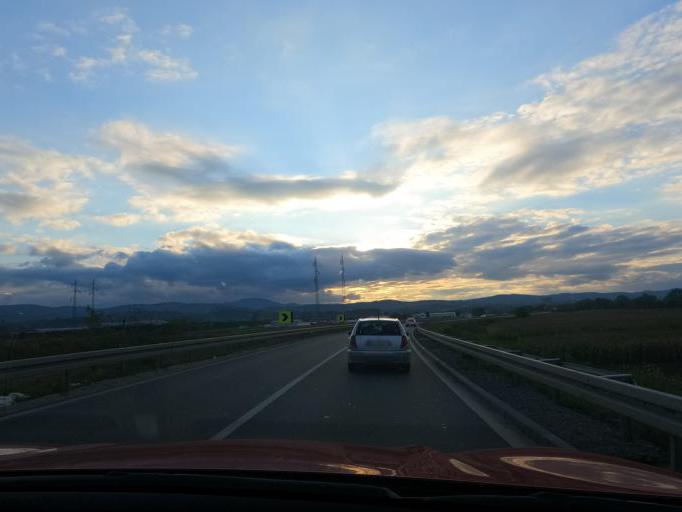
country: RS
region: Central Serbia
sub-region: Zlatiborski Okrug
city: Pozega
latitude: 43.8374
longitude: 20.0496
